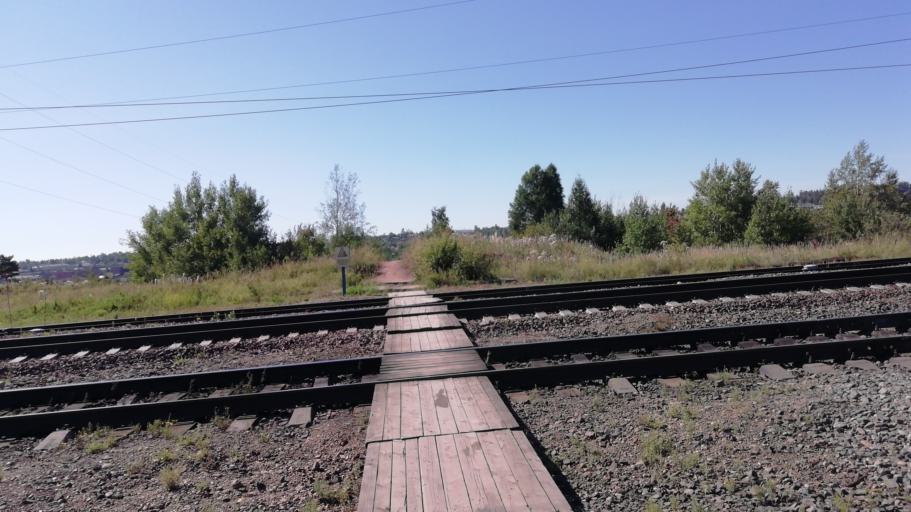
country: RU
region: Irkutsk
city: Bratsk
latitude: 56.3093
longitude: 101.7077
